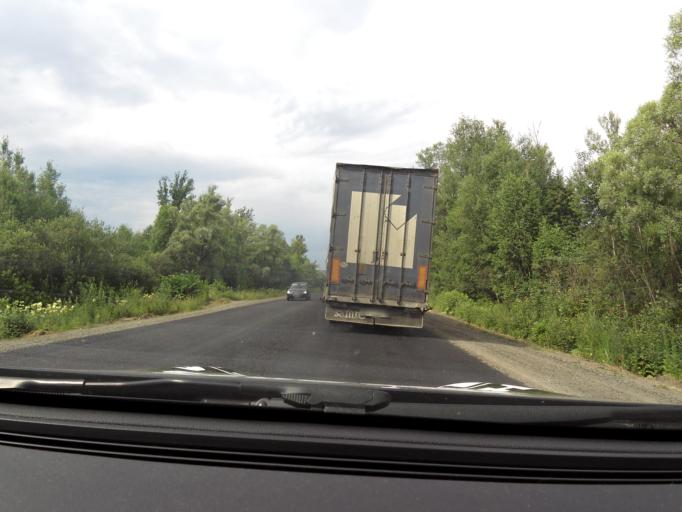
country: RU
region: Chelyabinsk
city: Asha
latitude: 54.8635
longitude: 57.1647
